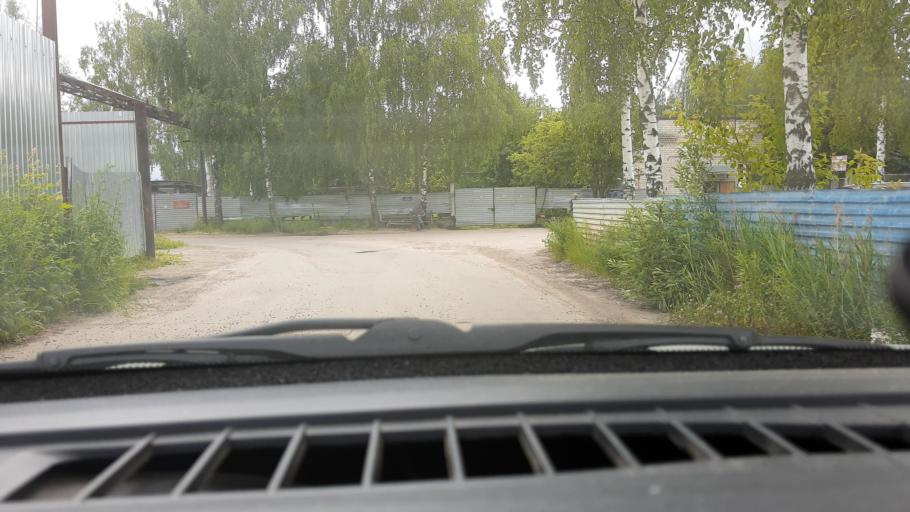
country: RU
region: Nizjnij Novgorod
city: Gorbatovka
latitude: 56.3201
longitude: 43.8461
